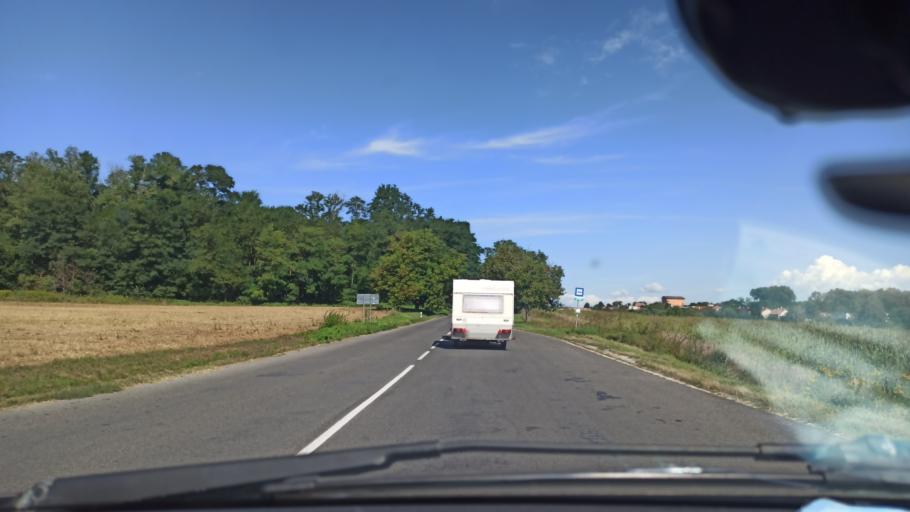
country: SK
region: Trnavsky
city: Gbely
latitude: 48.6657
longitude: 17.2077
